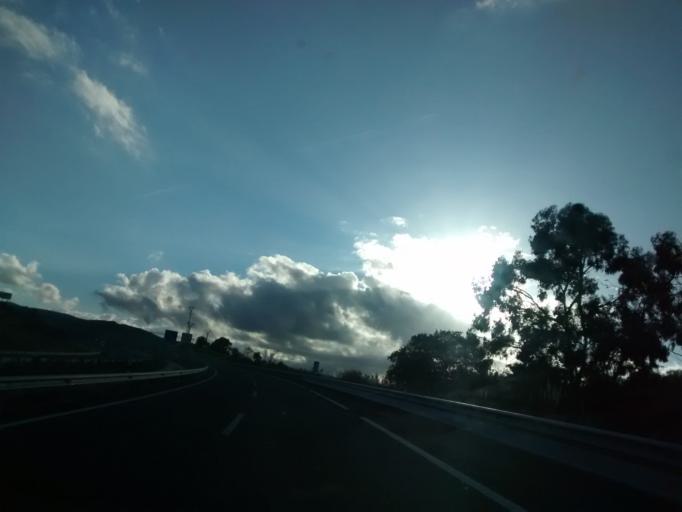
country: ES
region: Cantabria
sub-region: Provincia de Cantabria
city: Lierganes
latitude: 43.3736
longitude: -3.7547
